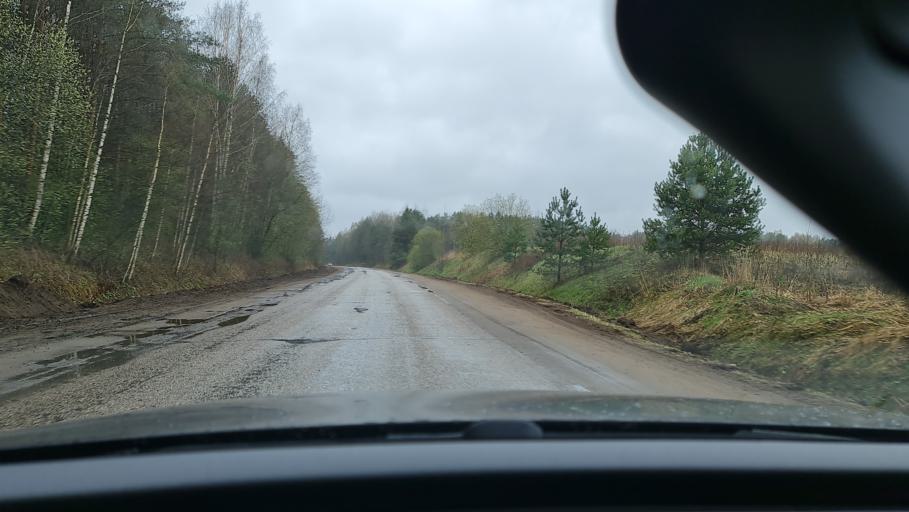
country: RU
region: Novgorod
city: Valday
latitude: 58.0408
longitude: 32.9204
